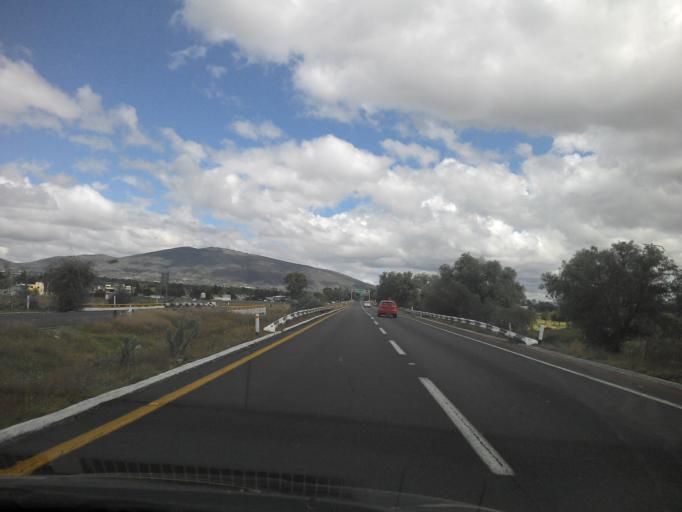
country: MX
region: Morelos
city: Teotihuacan de Arista
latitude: 19.6721
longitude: -98.8660
